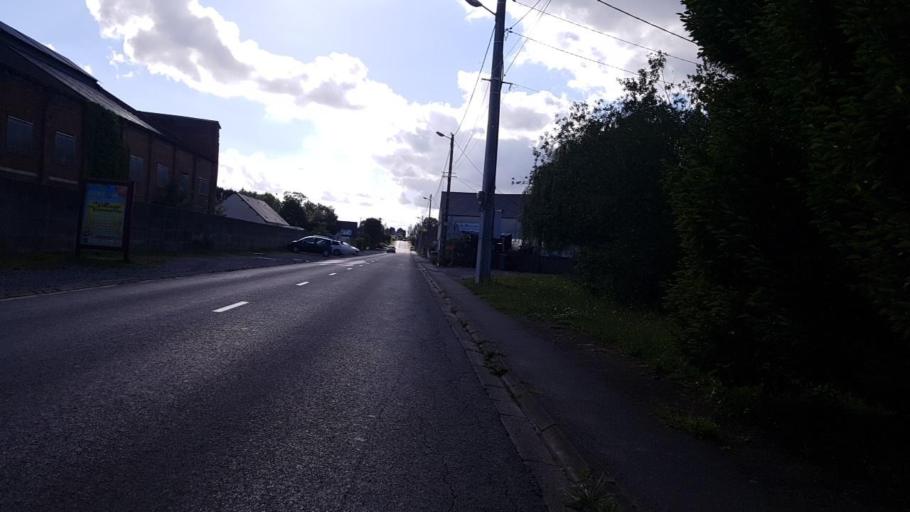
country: FR
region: Picardie
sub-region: Departement de l'Aisne
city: Hirson
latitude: 49.9205
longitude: 4.0738
